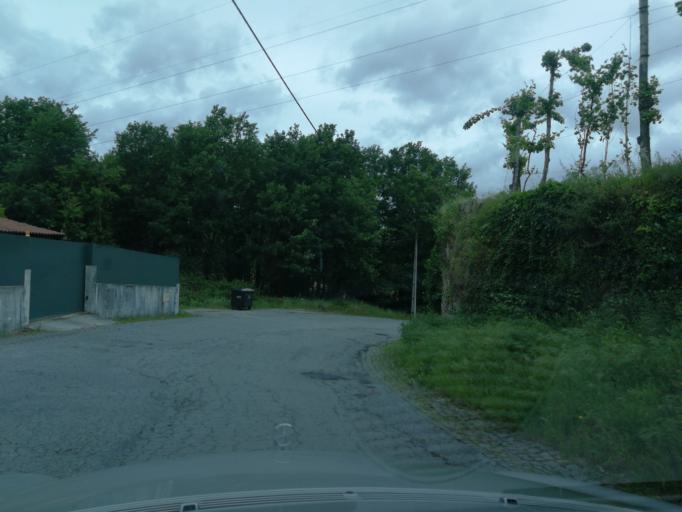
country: PT
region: Braga
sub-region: Braga
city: Adaufe
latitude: 41.6039
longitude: -8.4085
